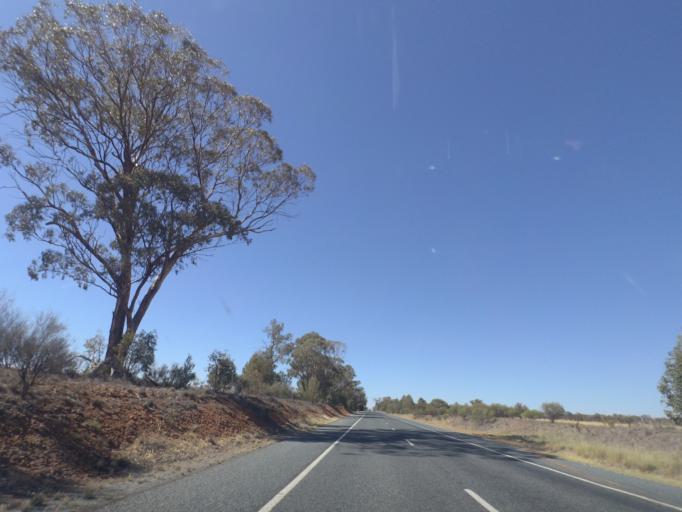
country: AU
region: New South Wales
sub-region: Bland
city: West Wyalong
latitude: -34.1619
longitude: 147.1166
